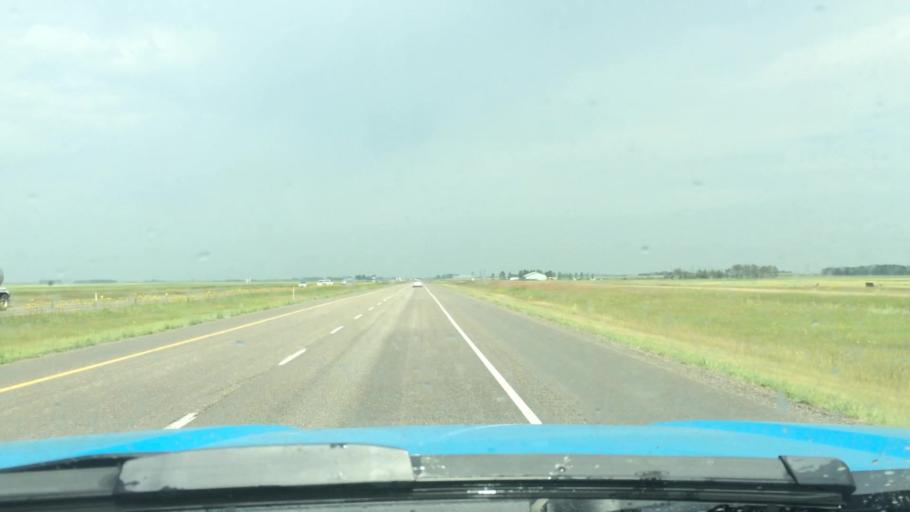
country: CA
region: Alberta
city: Didsbury
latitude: 51.6928
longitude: -114.0253
